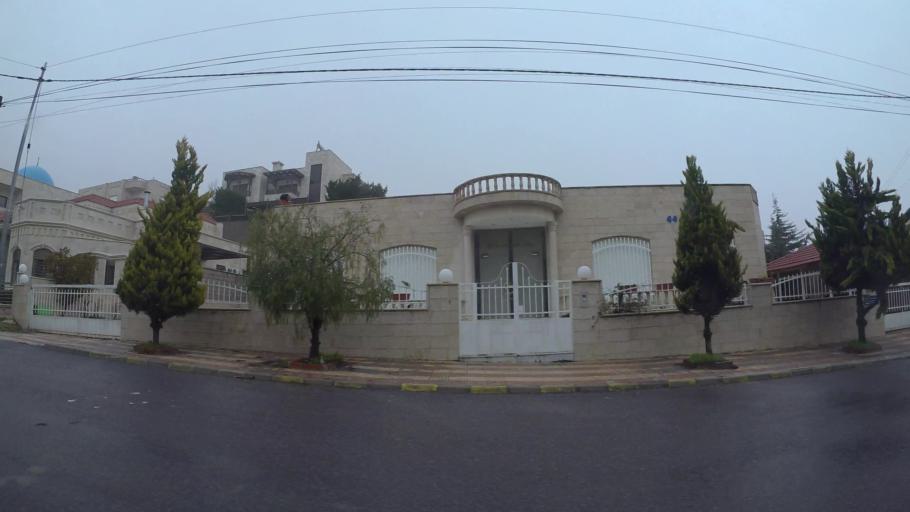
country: JO
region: Amman
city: Al Jubayhah
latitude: 32.0166
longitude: 35.8366
